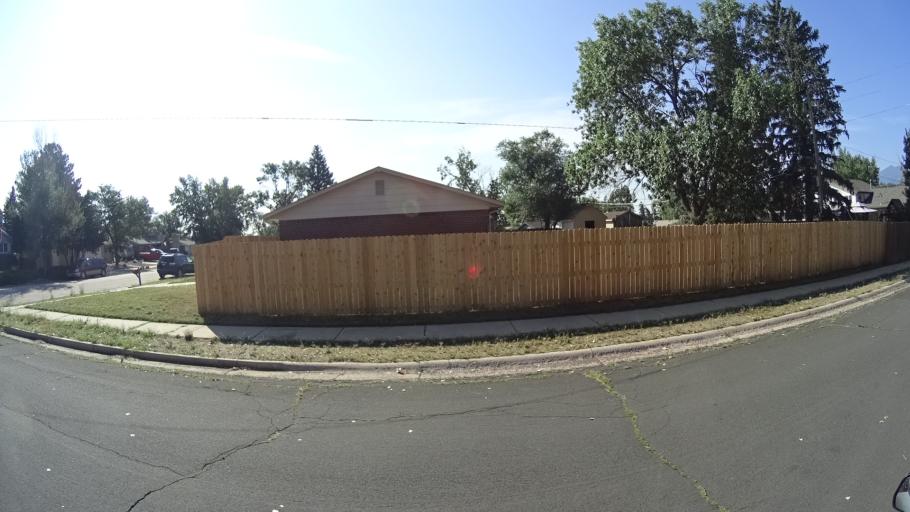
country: US
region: Colorado
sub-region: El Paso County
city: Colorado Springs
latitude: 38.8889
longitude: -104.8386
